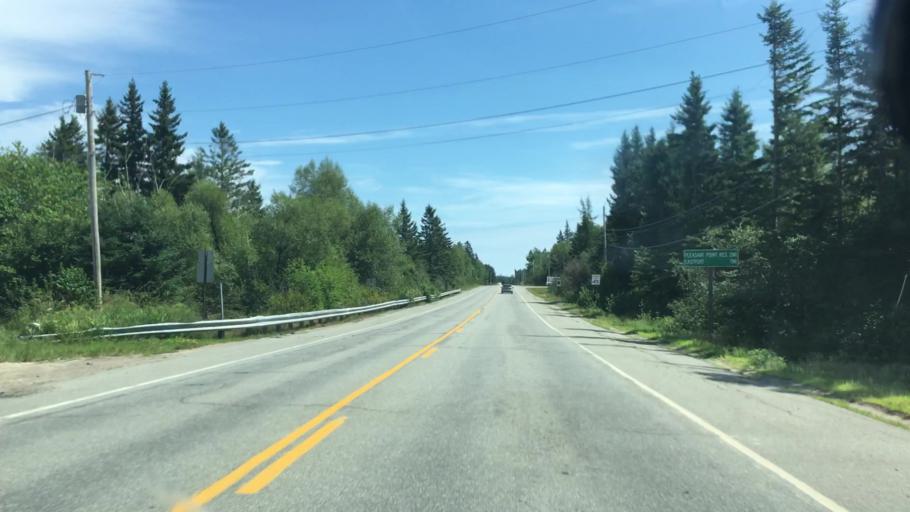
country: US
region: Maine
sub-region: Washington County
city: Eastport
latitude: 44.9697
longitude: -67.0740
